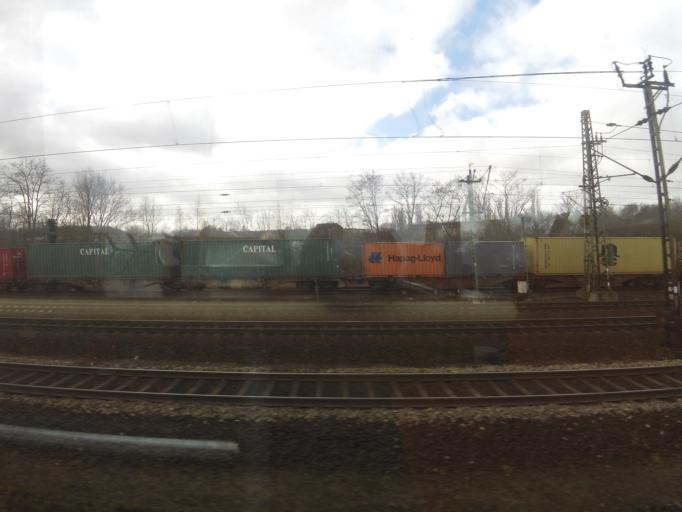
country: DE
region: Hamburg
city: Harburg
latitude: 53.4435
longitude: 10.0076
